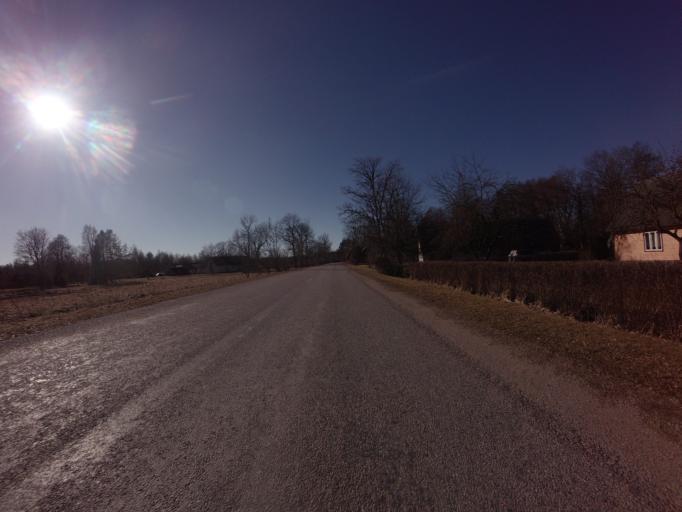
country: EE
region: Saare
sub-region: Kuressaare linn
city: Kuressaare
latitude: 58.5735
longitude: 22.5224
